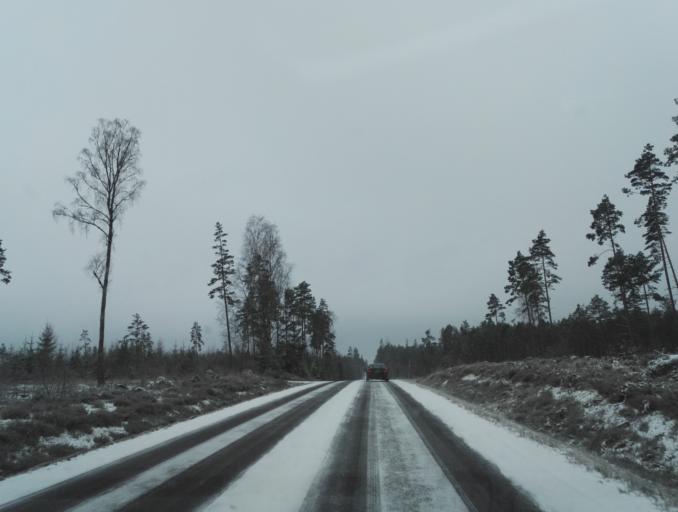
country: SE
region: Kronoberg
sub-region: Lessebo Kommun
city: Lessebo
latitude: 56.7726
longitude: 15.2977
